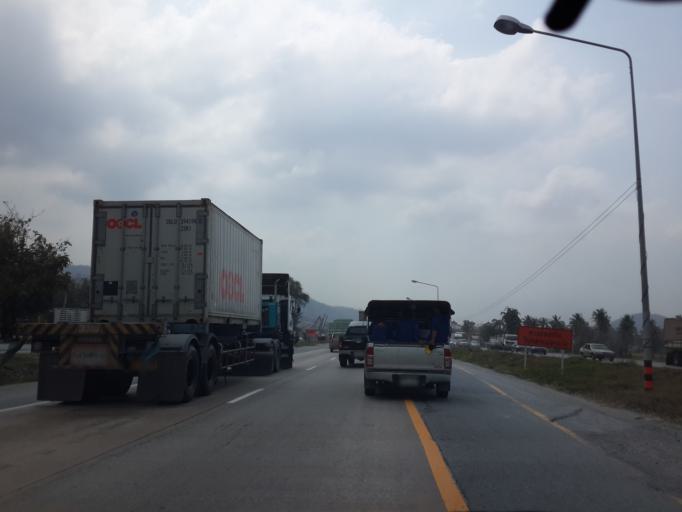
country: TH
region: Chon Buri
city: Chon Buri
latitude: 13.3128
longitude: 100.9926
